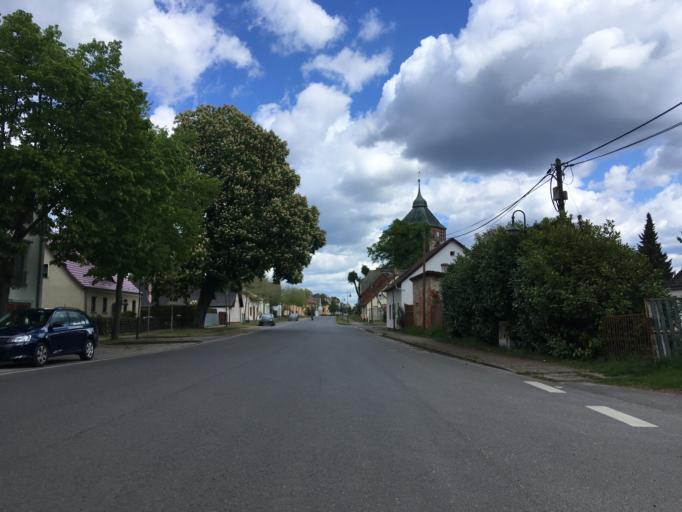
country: DE
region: Brandenburg
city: Marienwerder
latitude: 52.9053
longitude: 13.5285
